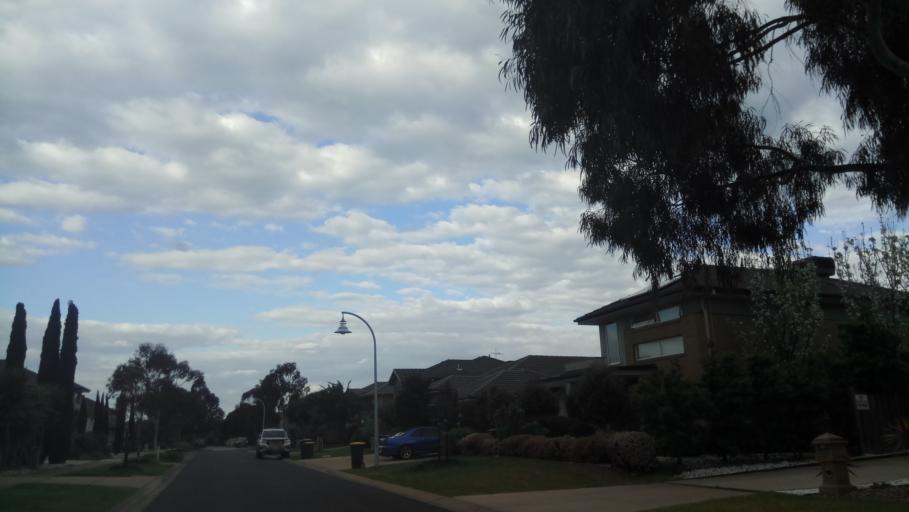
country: AU
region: Victoria
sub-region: Hobsons Bay
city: Altona Meadows
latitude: -37.8926
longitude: 144.7744
